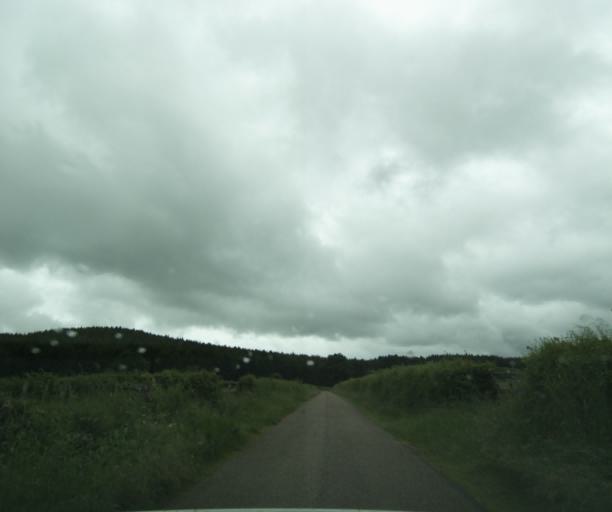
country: FR
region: Bourgogne
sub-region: Departement de Saone-et-Loire
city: Matour
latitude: 46.4344
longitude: 4.4446
